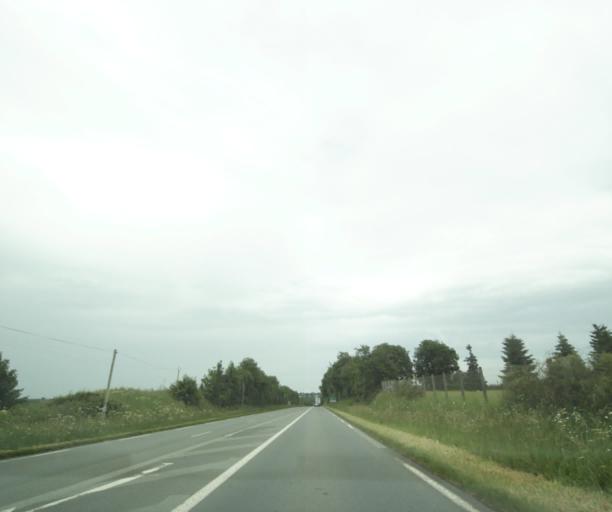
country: FR
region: Poitou-Charentes
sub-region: Departement des Deux-Sevres
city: Saint-Pardoux
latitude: 46.5518
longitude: -0.3097
